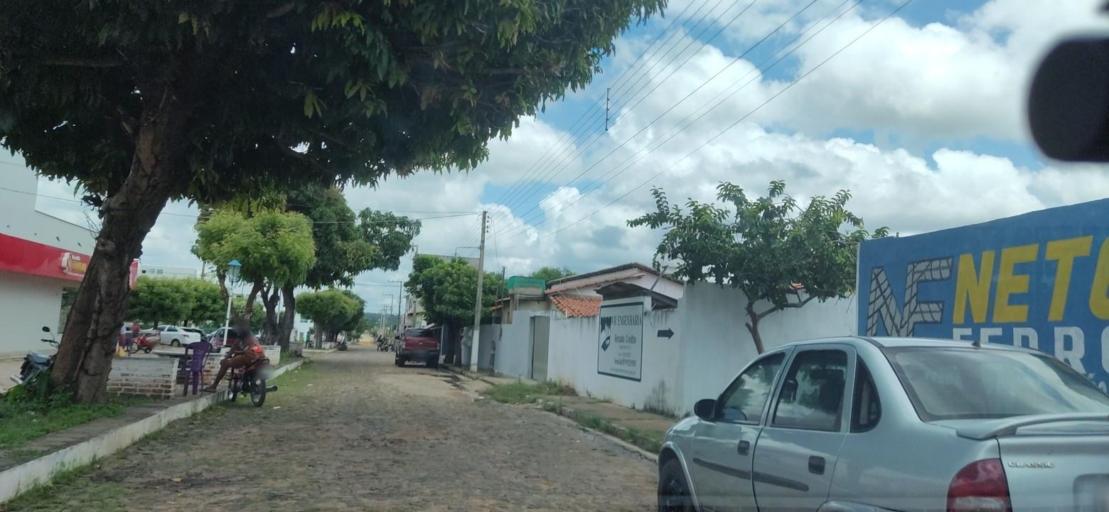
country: BR
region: Piaui
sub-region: Valenca Do Piaui
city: Valenca do Piaui
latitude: -6.4008
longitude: -41.7366
